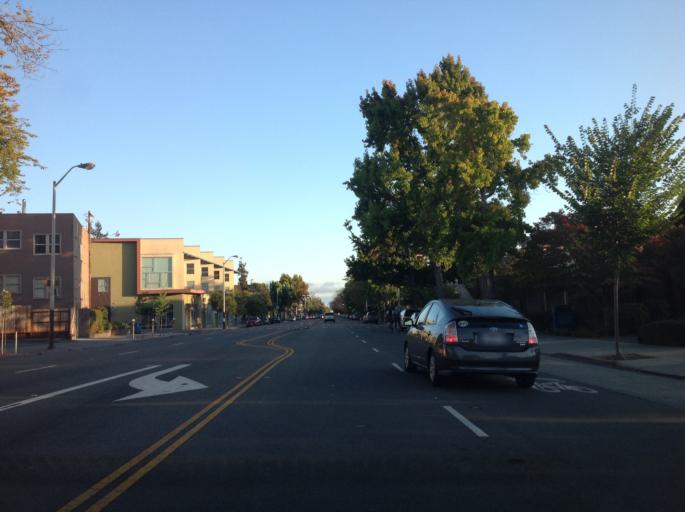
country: US
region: California
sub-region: Alameda County
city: Berkeley
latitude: 37.8552
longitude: -122.2599
